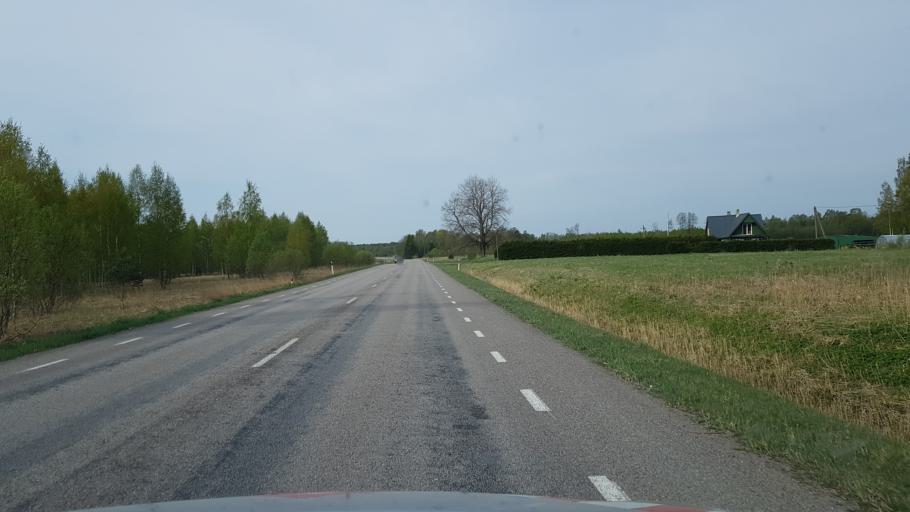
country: EE
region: Paernumaa
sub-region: Audru vald
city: Audru
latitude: 58.3978
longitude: 24.2909
